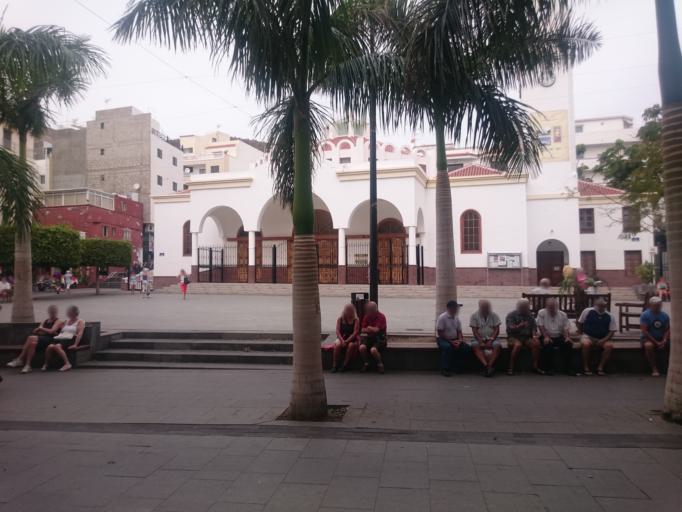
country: ES
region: Canary Islands
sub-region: Provincia de Santa Cruz de Tenerife
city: Playa de las Americas
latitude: 28.0517
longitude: -16.7171
